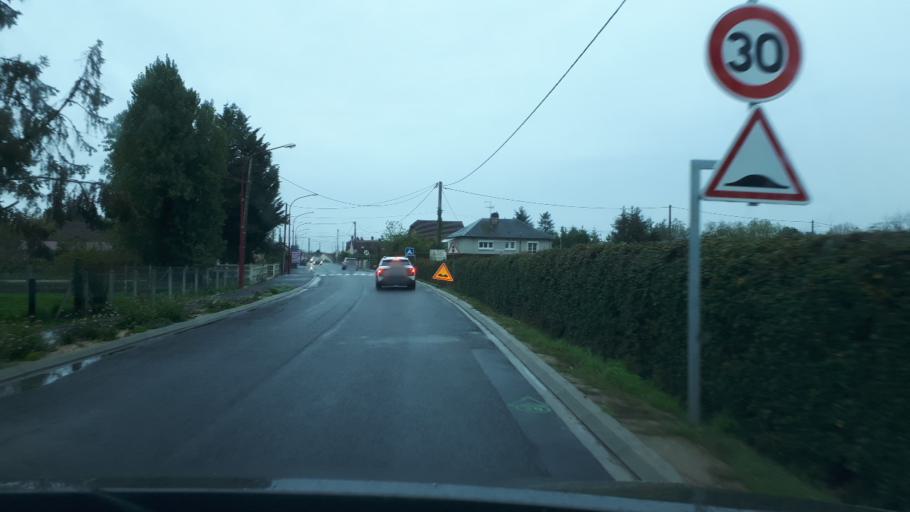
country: FR
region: Centre
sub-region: Departement du Loir-et-Cher
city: Gievres
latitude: 47.2812
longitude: 1.6669
